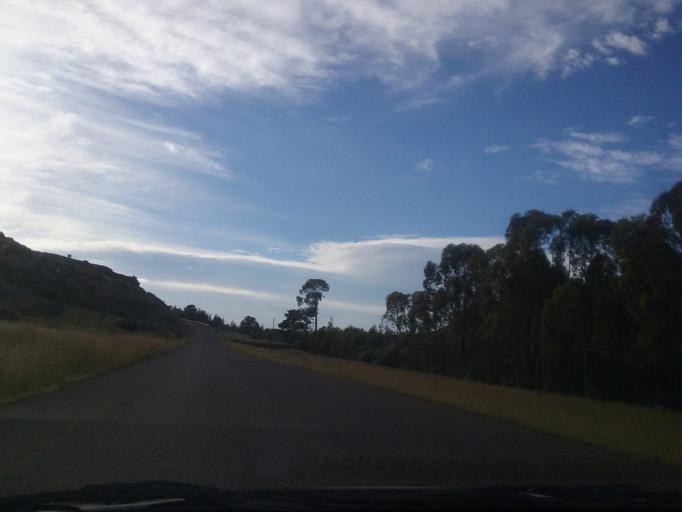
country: LS
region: Quthing
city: Quthing
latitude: -30.3887
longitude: 27.6088
